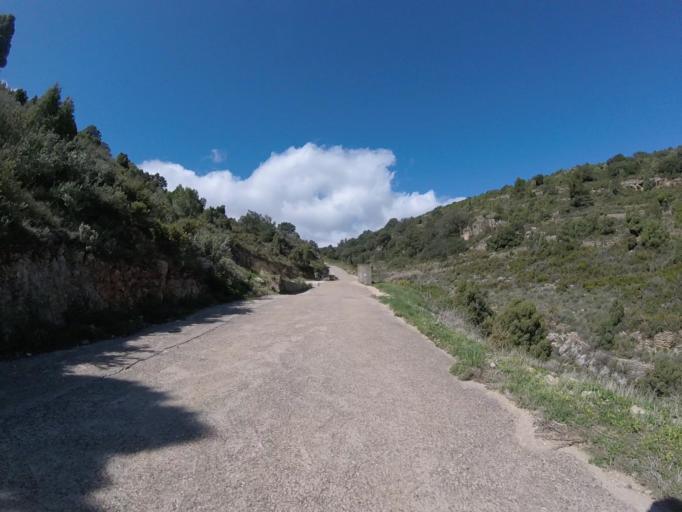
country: ES
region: Valencia
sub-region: Provincia de Castello
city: Culla
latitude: 40.3145
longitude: -0.0980
